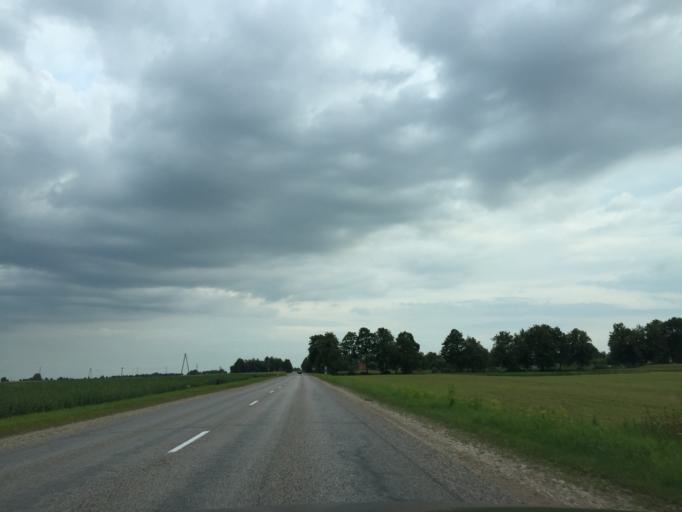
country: LV
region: Dobeles Rajons
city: Dobele
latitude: 56.5720
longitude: 23.2987
